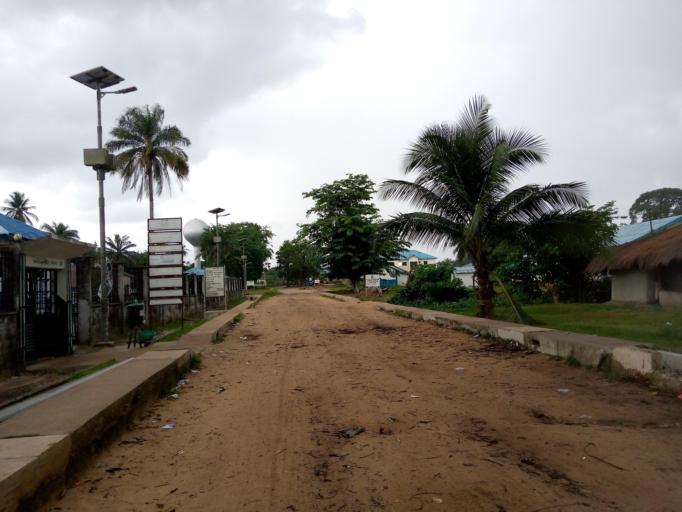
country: SL
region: Southern Province
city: Bonthe
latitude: 7.5293
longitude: -12.5063
